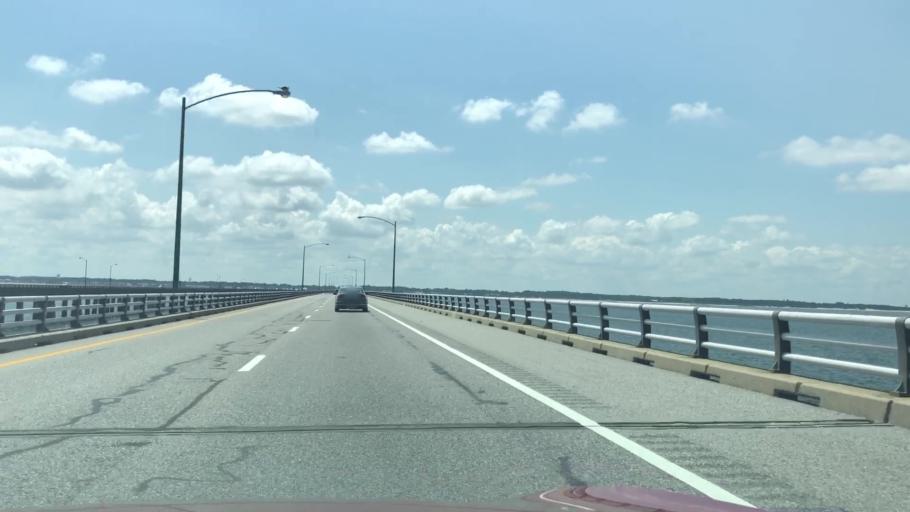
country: US
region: Virginia
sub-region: City of Virginia Beach
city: Virginia Beach
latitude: 36.9449
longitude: -76.1213
